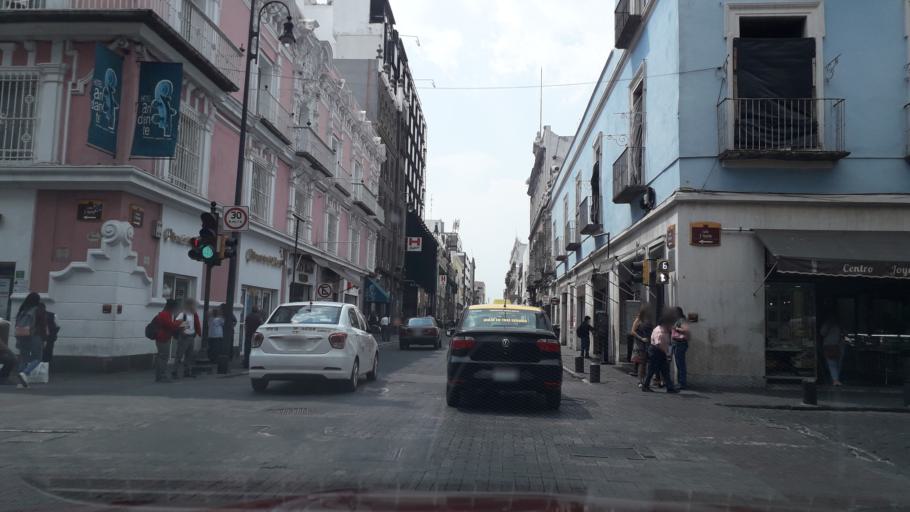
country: MX
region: Puebla
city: Puebla
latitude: 19.0443
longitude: -98.1965
